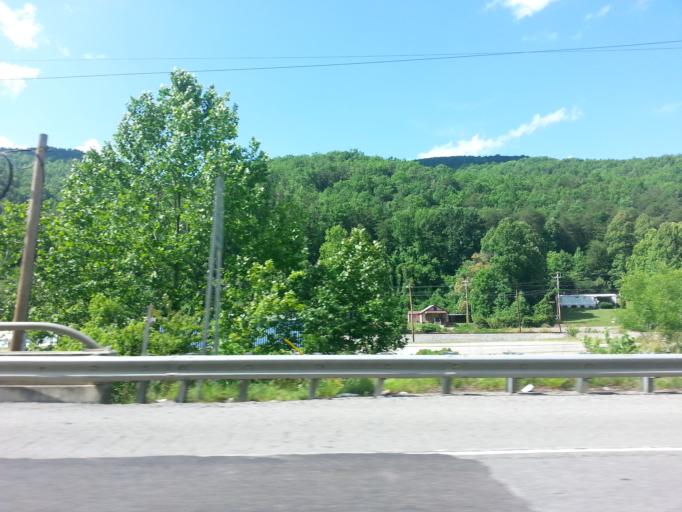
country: US
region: Kentucky
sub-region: Harlan County
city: Cumberland
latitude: 36.9456
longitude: -83.1093
